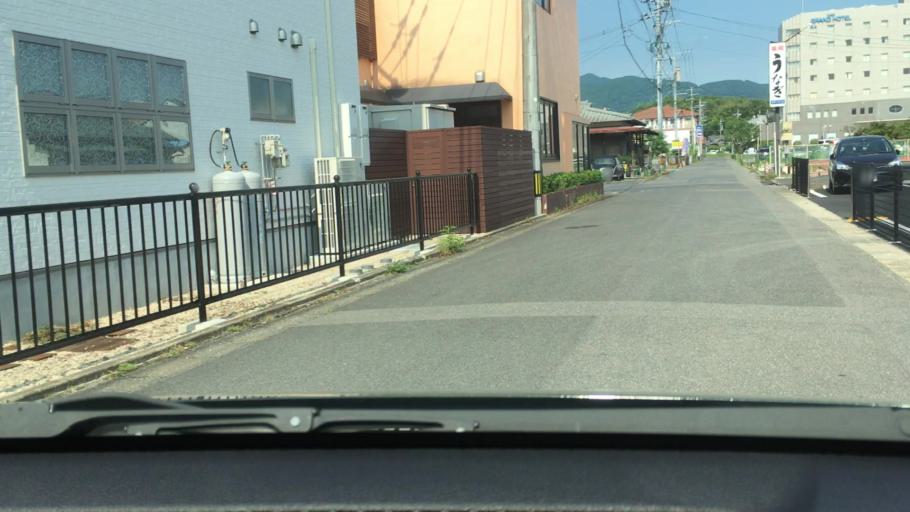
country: JP
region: Saga Prefecture
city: Imaricho-ko
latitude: 33.2700
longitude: 129.8730
